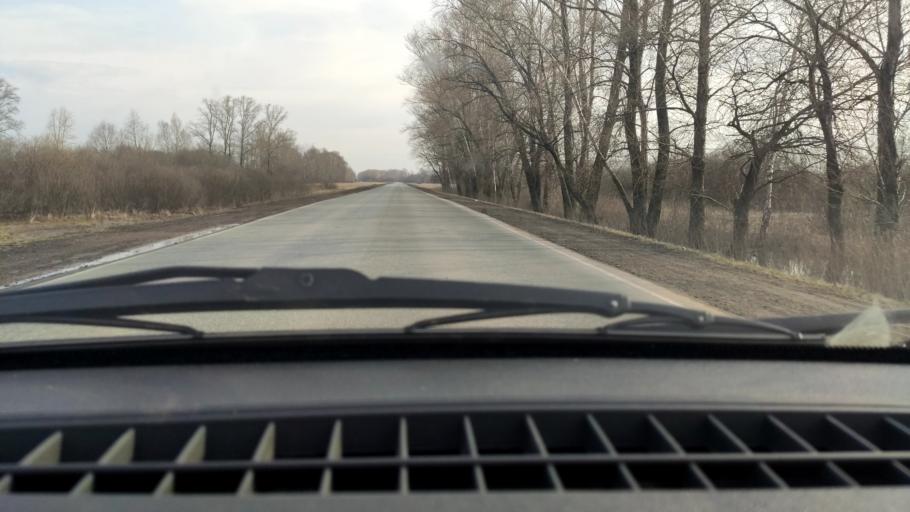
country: RU
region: Bashkortostan
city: Chishmy
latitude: 54.4029
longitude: 55.2146
